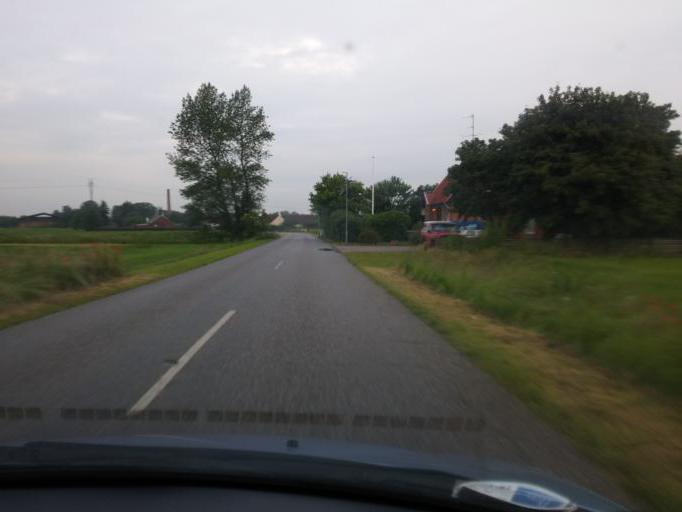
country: DK
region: South Denmark
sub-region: Kerteminde Kommune
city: Munkebo
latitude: 55.4057
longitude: 10.5367
